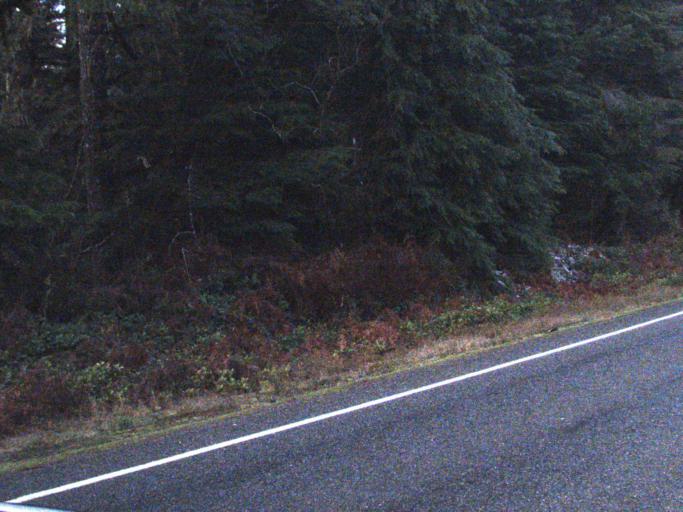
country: US
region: Washington
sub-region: Snohomish County
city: Darrington
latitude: 48.3594
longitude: -121.5398
